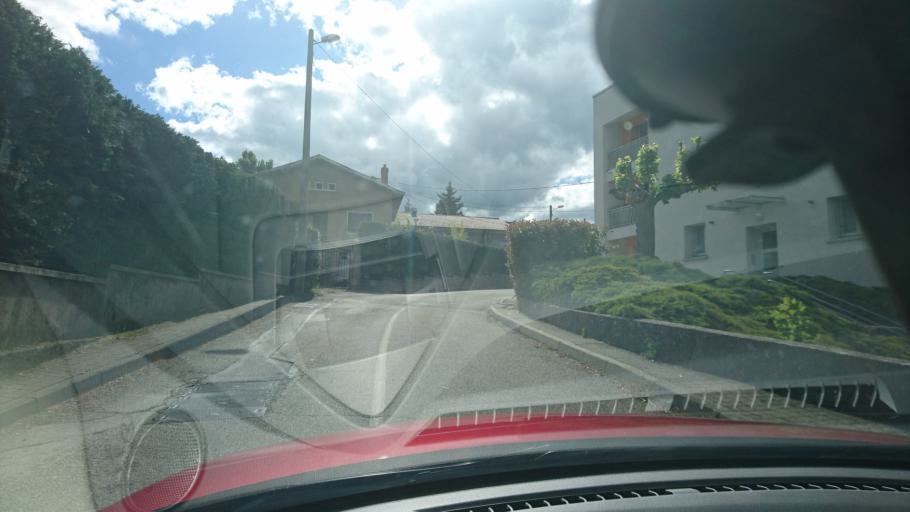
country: FR
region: Rhone-Alpes
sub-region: Departement de la Loire
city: Saint-Pierre-de-Boeuf
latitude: 45.3814
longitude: 4.7482
